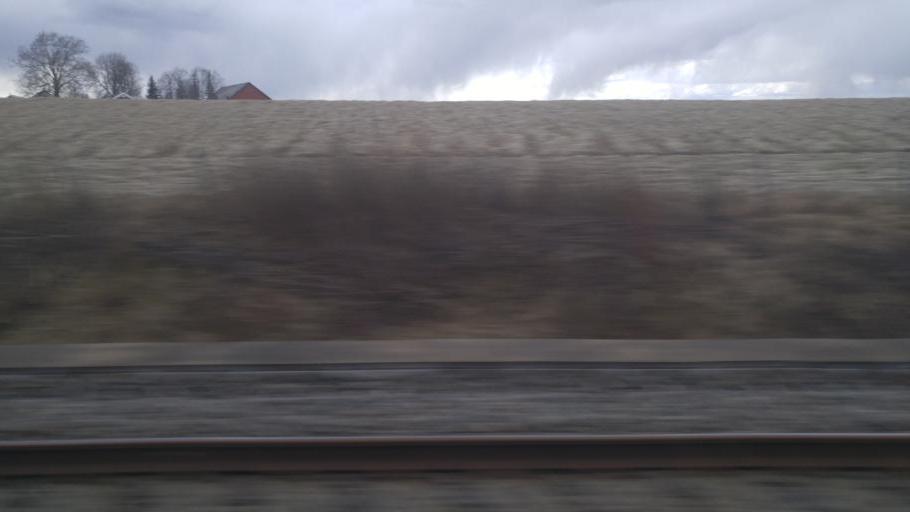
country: NO
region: Akershus
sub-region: Ullensaker
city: Jessheim
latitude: 60.1307
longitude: 11.1587
